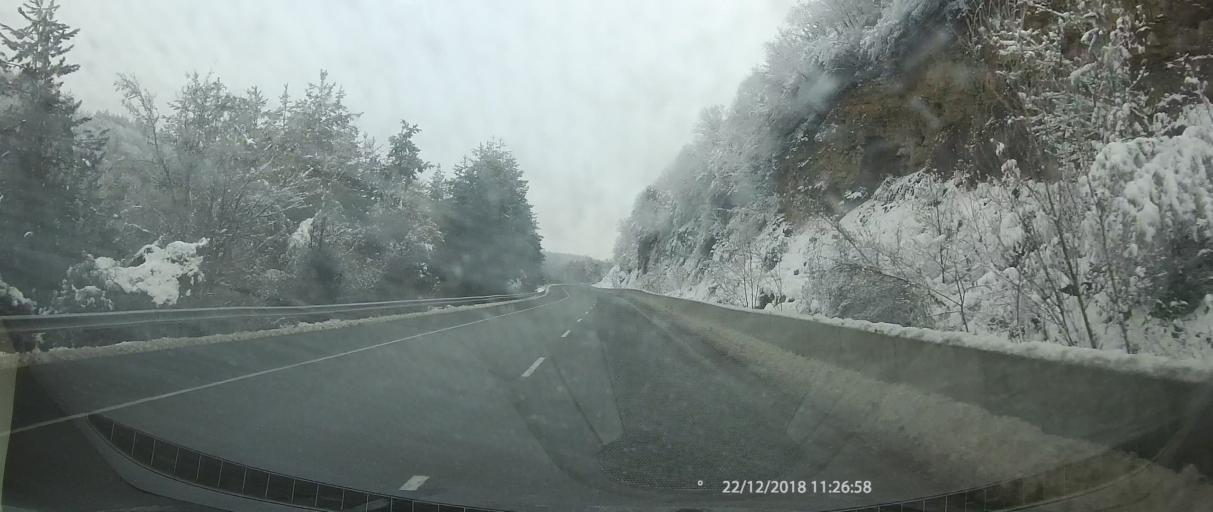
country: BG
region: Kyustendil
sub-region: Obshtina Bobovdol
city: Bobovdol
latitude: 42.2721
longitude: 22.9267
